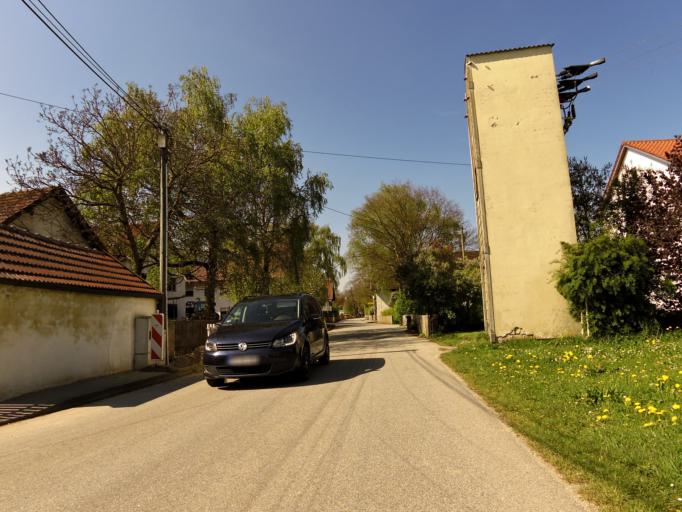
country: DE
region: Bavaria
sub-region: Upper Bavaria
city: Wartenberg
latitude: 48.3964
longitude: 11.9652
